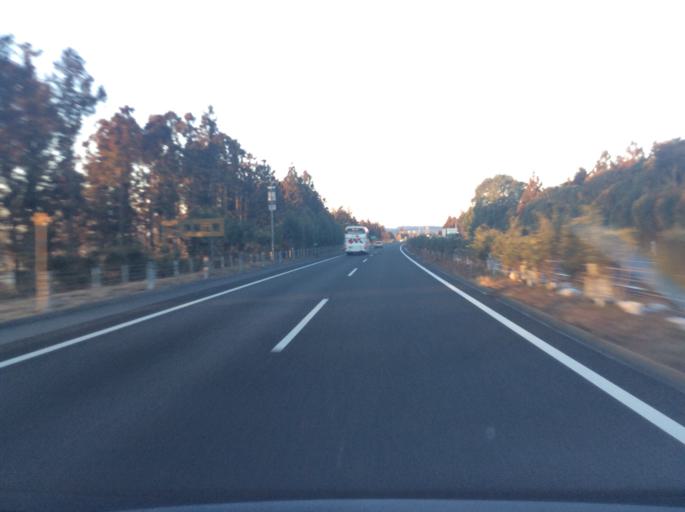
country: JP
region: Ibaraki
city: Mito-shi
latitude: 36.4306
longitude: 140.4459
